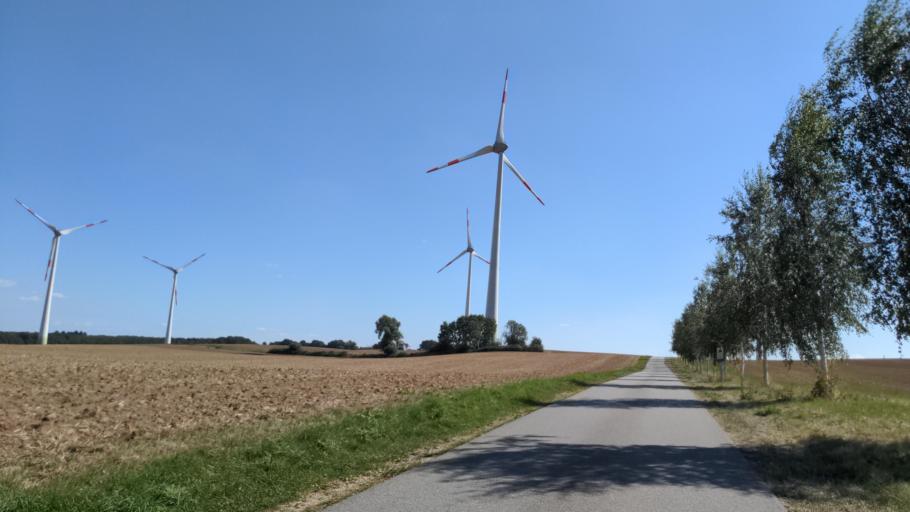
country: DE
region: Mecklenburg-Vorpommern
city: Selmsdorf
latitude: 53.8778
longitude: 10.8960
